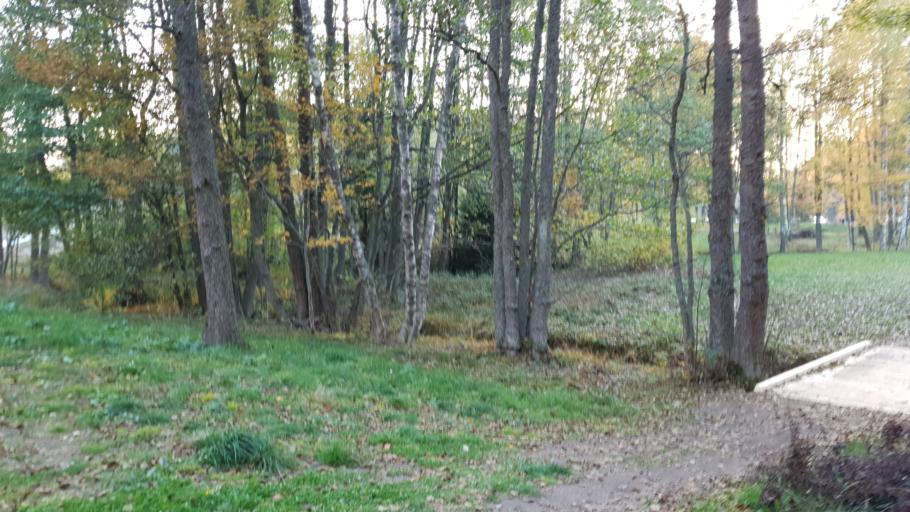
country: SE
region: Stockholm
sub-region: Tyreso Kommun
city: Bollmora
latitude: 59.1705
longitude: 18.2382
